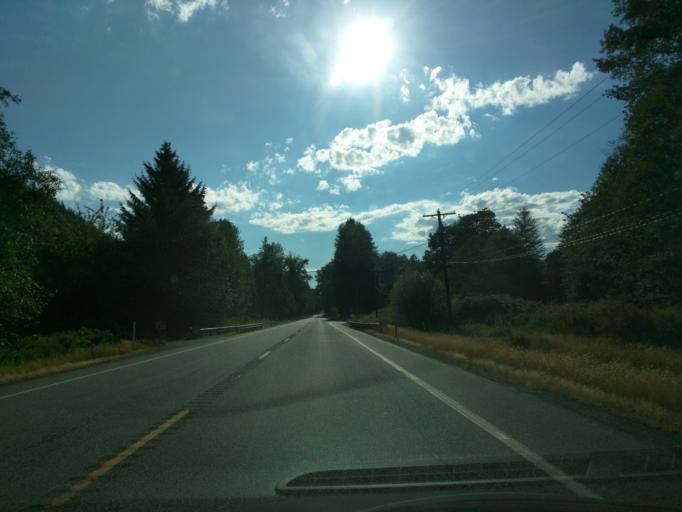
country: US
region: Washington
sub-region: Snohomish County
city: Darrington
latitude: 48.2769
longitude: -121.7995
